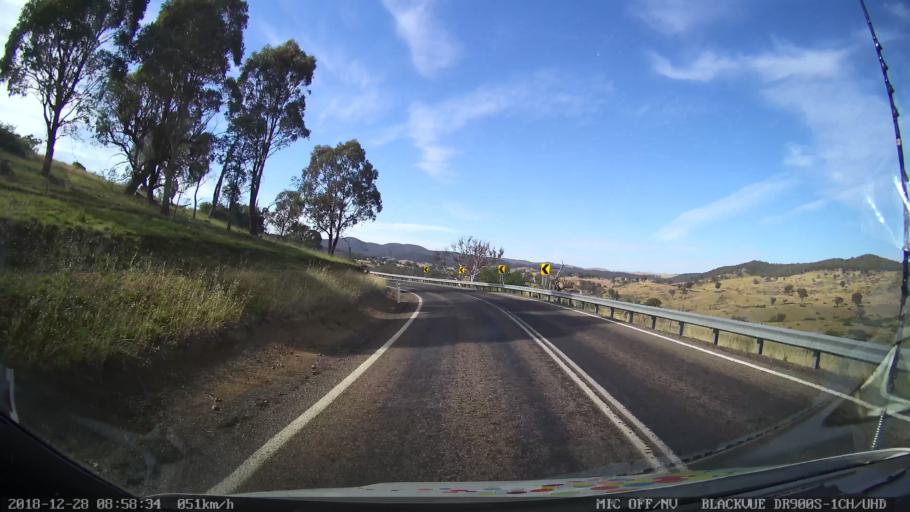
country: AU
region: New South Wales
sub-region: Upper Lachlan Shire
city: Crookwell
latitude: -34.1281
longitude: 149.3321
